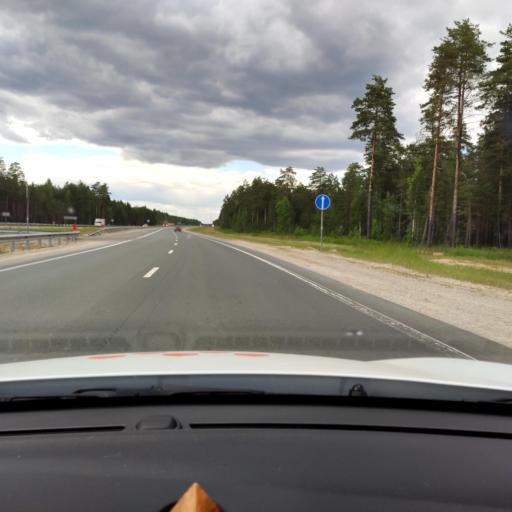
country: RU
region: Mariy-El
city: Surok
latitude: 56.4515
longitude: 48.1008
